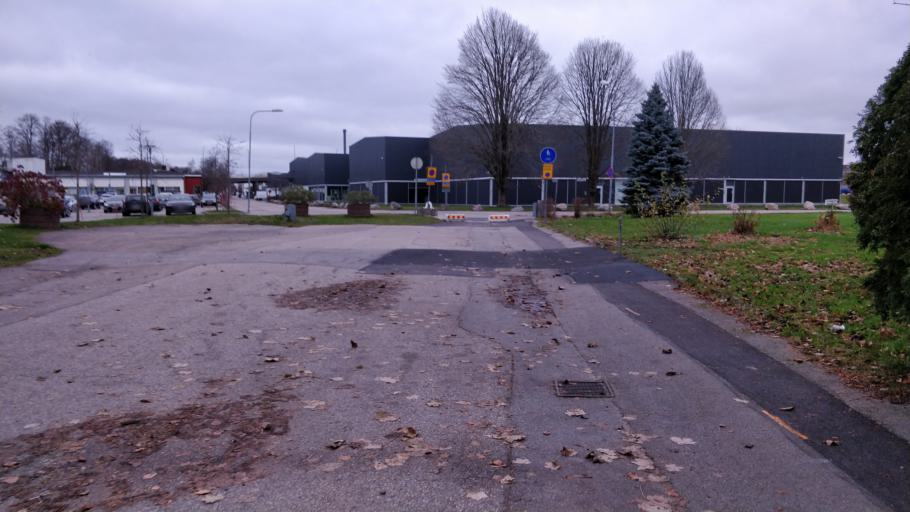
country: SE
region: Kronoberg
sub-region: Almhults Kommun
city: AElmhult
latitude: 56.5483
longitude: 14.1324
